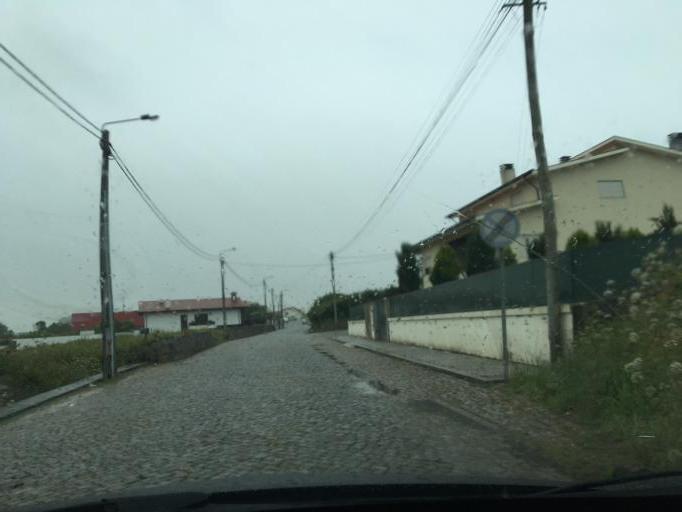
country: PT
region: Porto
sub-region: Maia
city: Anta
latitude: 41.2749
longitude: -8.6180
